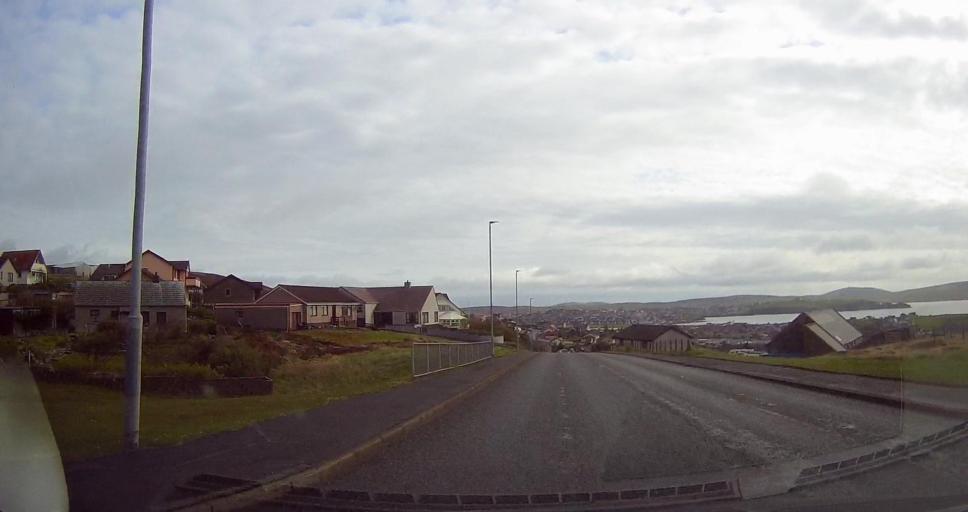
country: GB
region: Scotland
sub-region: Shetland Islands
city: Lerwick
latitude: 60.1418
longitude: -1.1838
